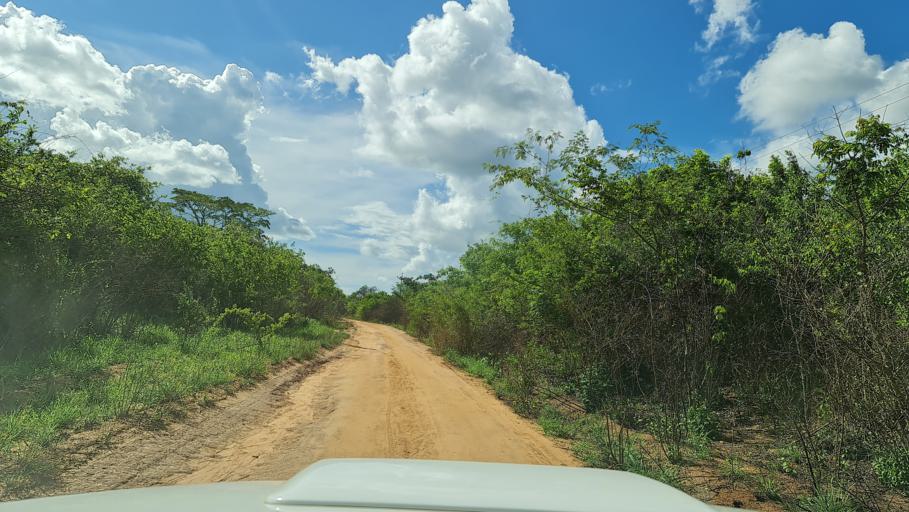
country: MZ
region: Nampula
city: Ilha de Mocambique
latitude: -15.4133
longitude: 40.2552
